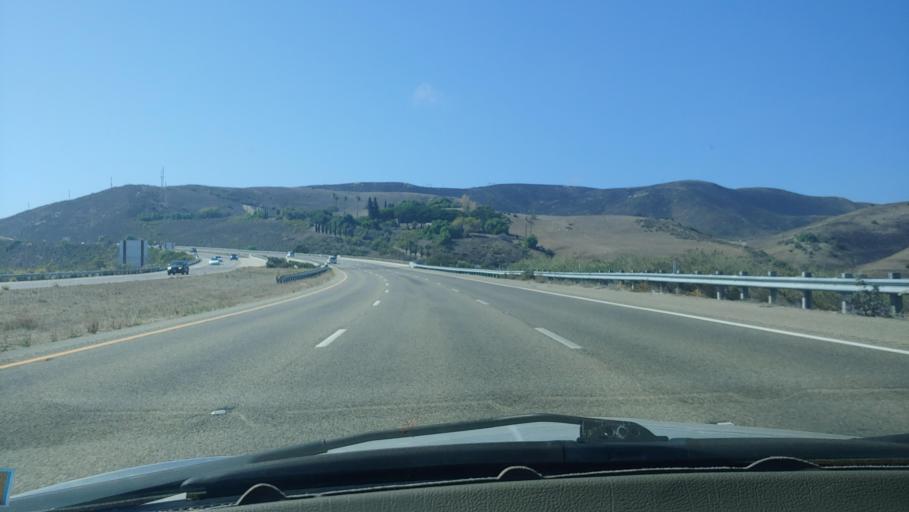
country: US
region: California
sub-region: Santa Barbara County
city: Solvang
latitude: 34.4656
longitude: -120.0669
